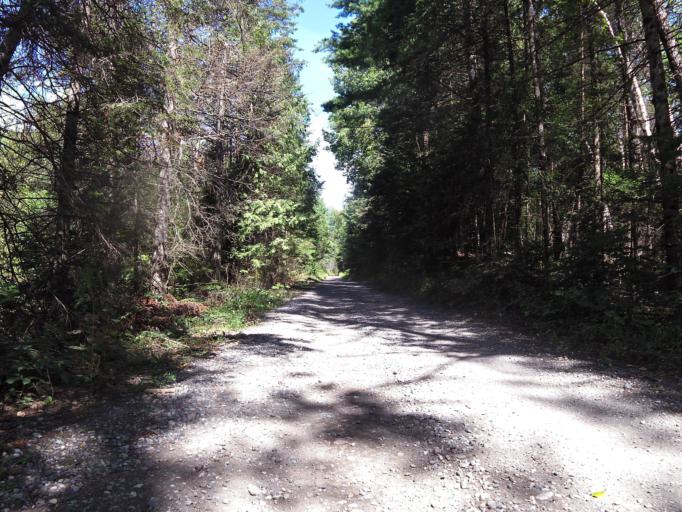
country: CA
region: Ontario
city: Renfrew
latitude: 45.0860
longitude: -76.7208
